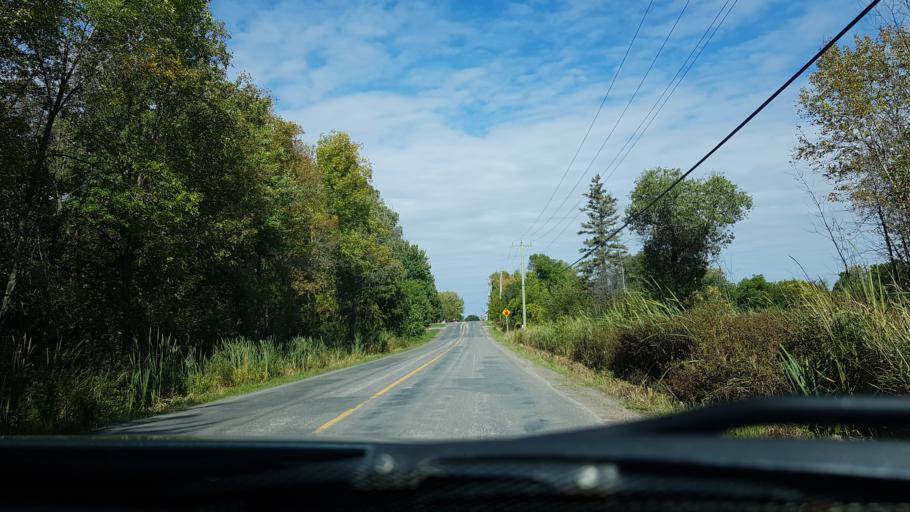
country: CA
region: Ontario
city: Orillia
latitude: 44.5953
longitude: -79.3186
